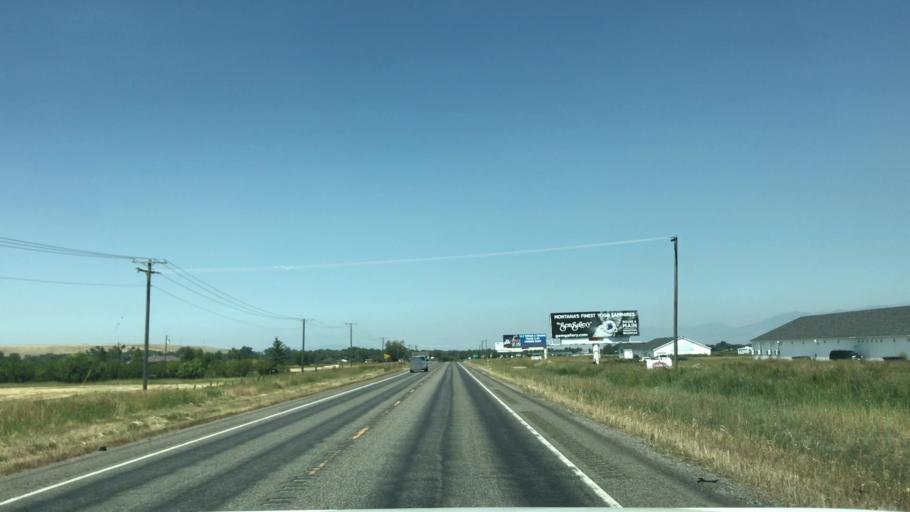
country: US
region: Montana
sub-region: Gallatin County
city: Four Corners
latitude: 45.6338
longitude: -111.1969
